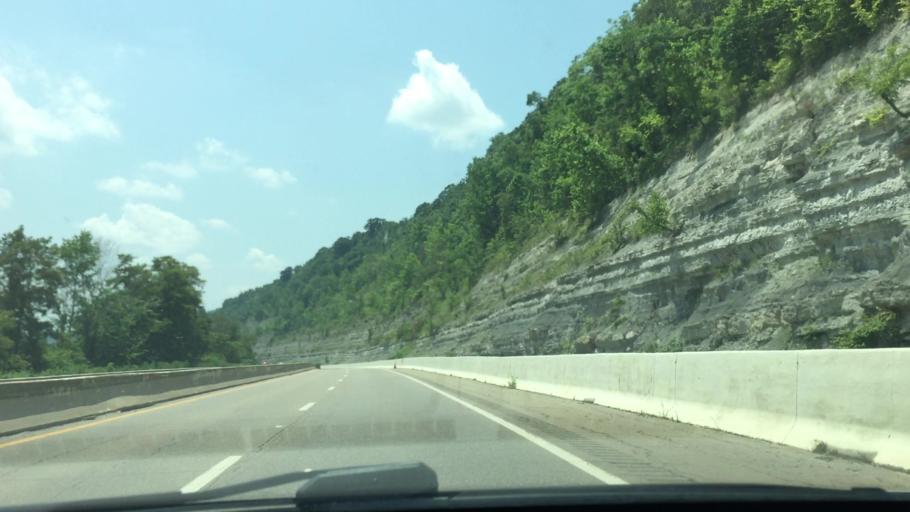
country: US
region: West Virginia
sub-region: Marshall County
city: Glendale
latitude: 39.9528
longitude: -80.7644
